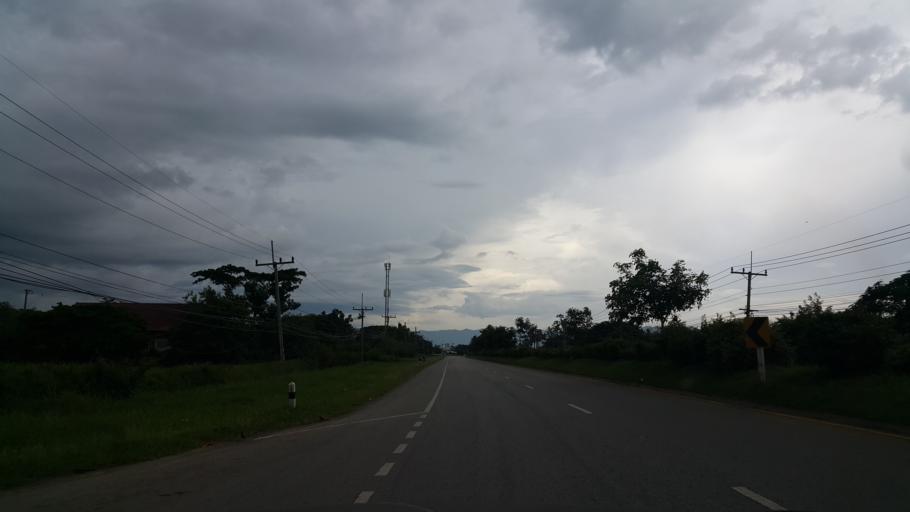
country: TH
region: Phayao
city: Dok Kham Tai
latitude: 19.1545
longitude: 99.9460
